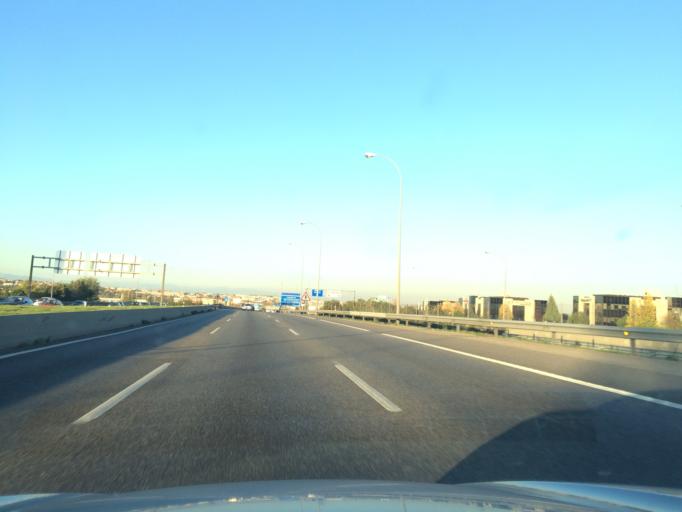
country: ES
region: Madrid
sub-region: Provincia de Madrid
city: Alcobendas
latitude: 40.5254
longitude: -3.6488
